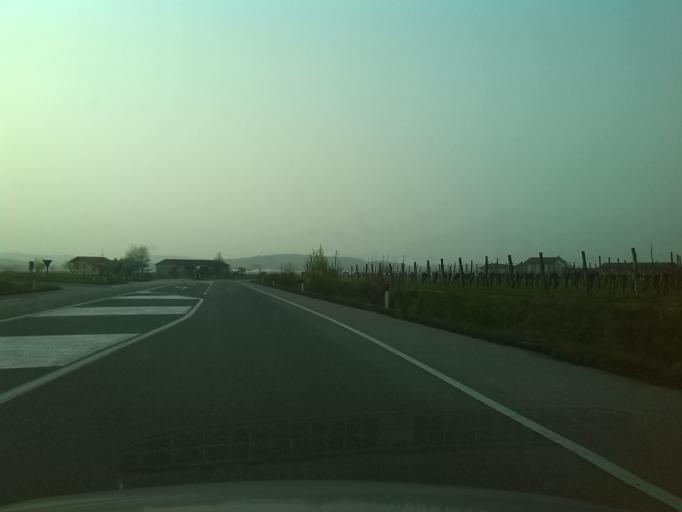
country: IT
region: Friuli Venezia Giulia
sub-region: Provincia di Udine
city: Cividale del Friuli
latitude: 46.0659
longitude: 13.4328
